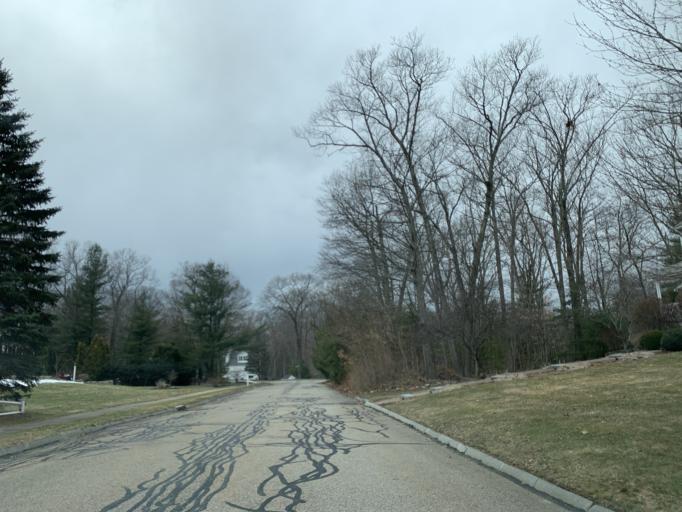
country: US
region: Massachusetts
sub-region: Norfolk County
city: Bellingham
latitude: 42.0458
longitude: -71.4524
